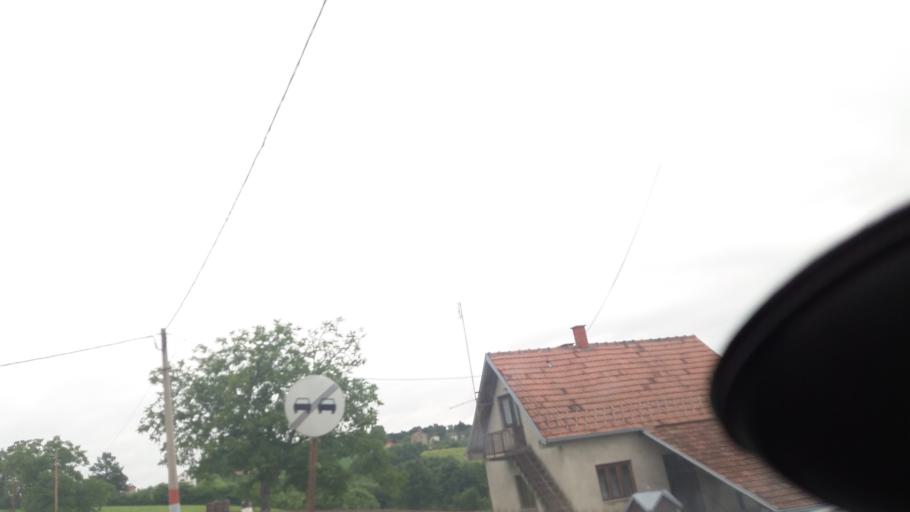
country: RS
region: Central Serbia
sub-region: Kolubarski Okrug
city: Ljig
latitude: 44.2216
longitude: 20.1768
